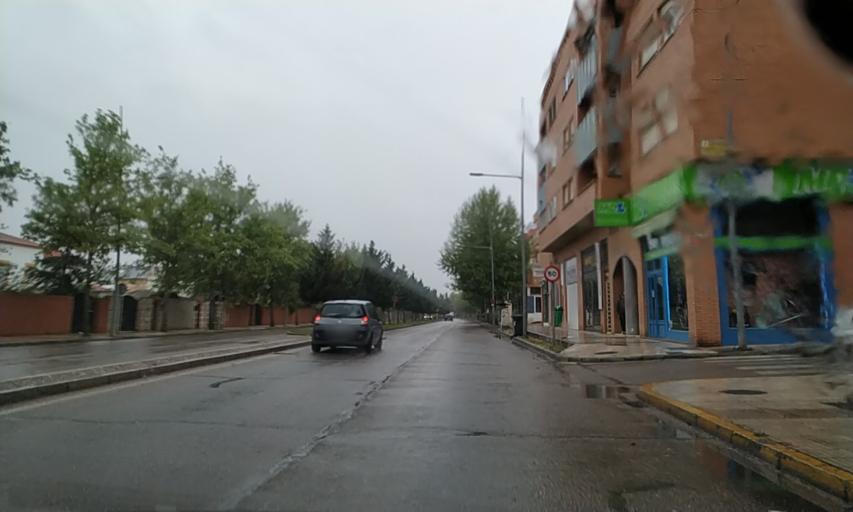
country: ES
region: Extremadura
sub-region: Provincia de Badajoz
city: Badajoz
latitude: 38.8654
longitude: -6.9729
